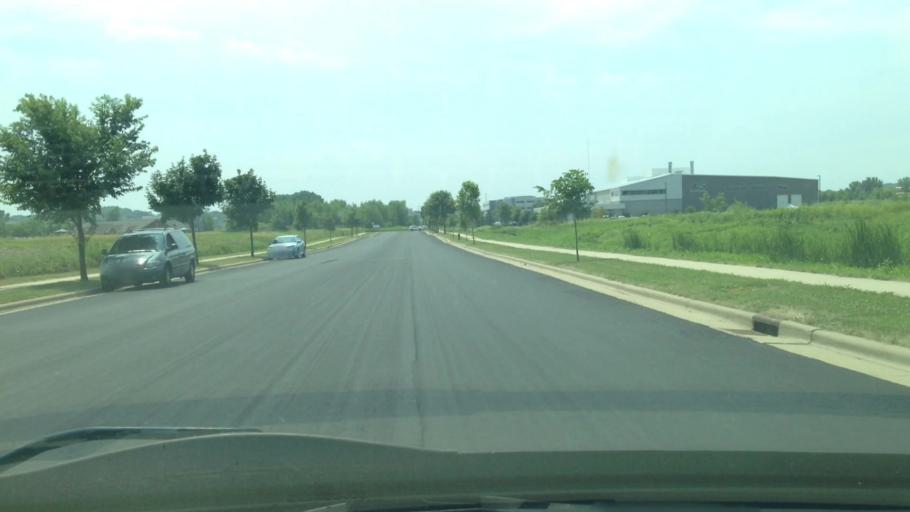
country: US
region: Wisconsin
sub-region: Dane County
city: Middleton
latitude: 43.1091
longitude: -89.5212
